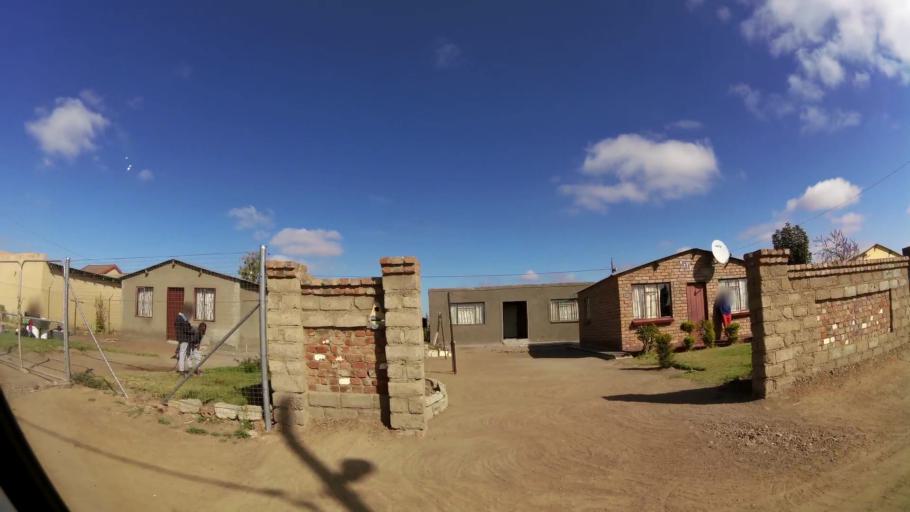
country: ZA
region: Limpopo
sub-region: Capricorn District Municipality
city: Polokwane
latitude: -23.8608
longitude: 29.3815
